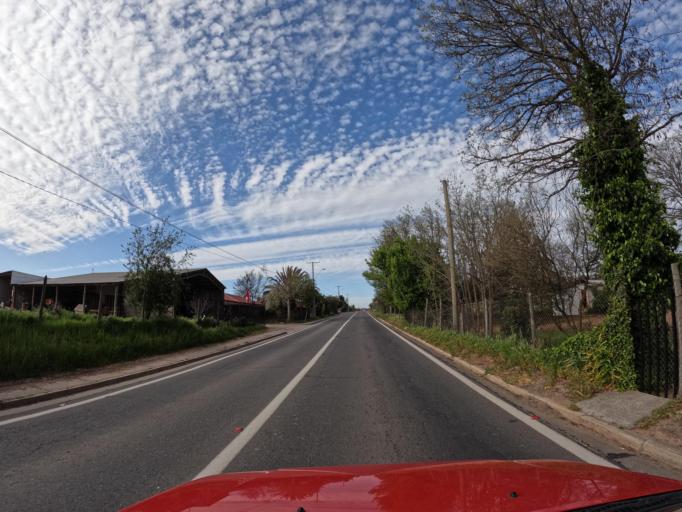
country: CL
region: O'Higgins
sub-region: Provincia de Colchagua
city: Santa Cruz
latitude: -34.2232
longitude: -71.7226
